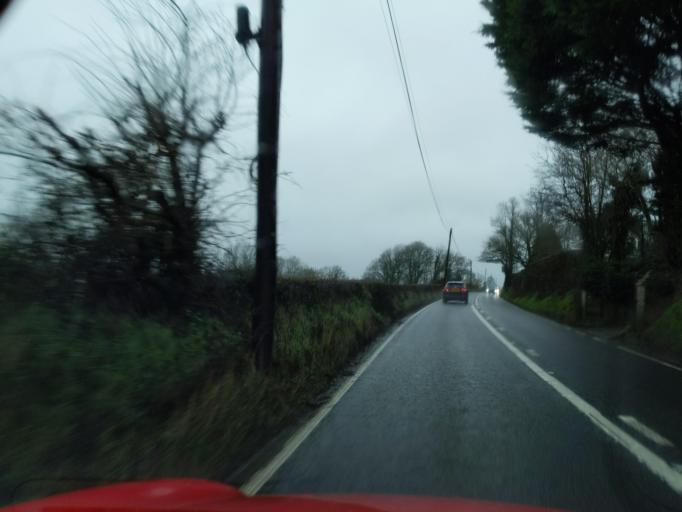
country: GB
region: England
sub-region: Cornwall
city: Launceston
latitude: 50.6051
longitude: -4.3387
